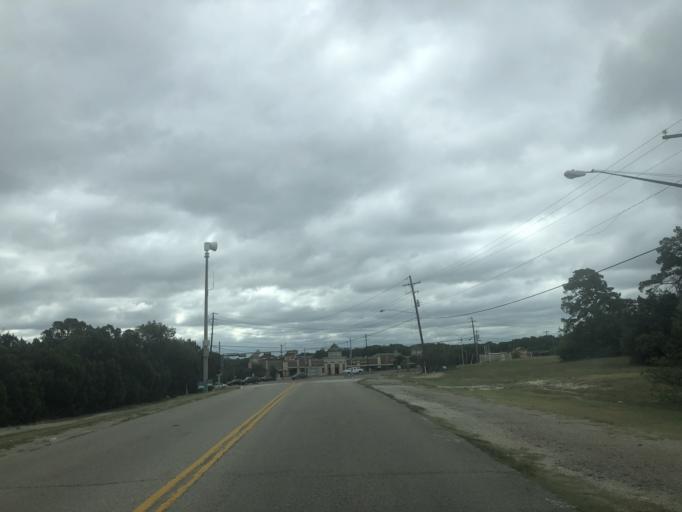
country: US
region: Texas
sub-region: Dallas County
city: Duncanville
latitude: 32.6630
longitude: -96.9445
